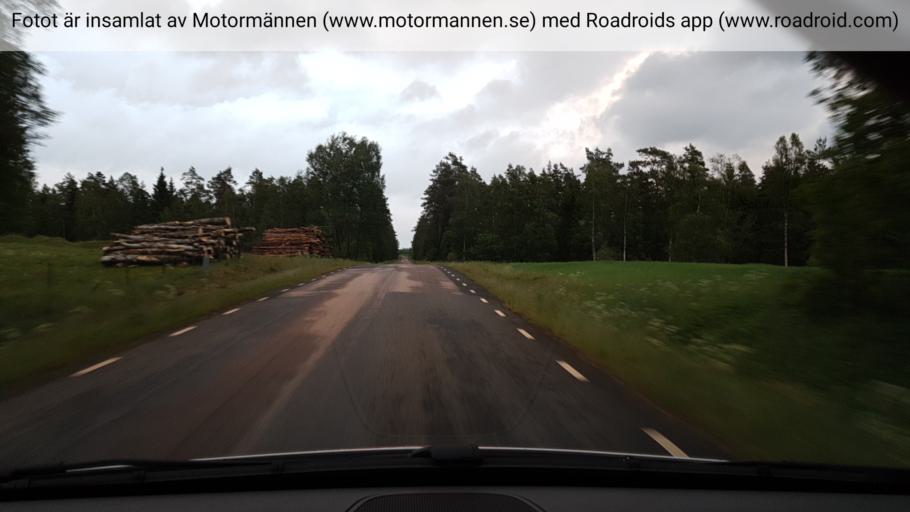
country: SE
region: Joenkoeping
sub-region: Vaggeryds Kommun
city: Skillingaryd
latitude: 57.3485
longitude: 14.0790
